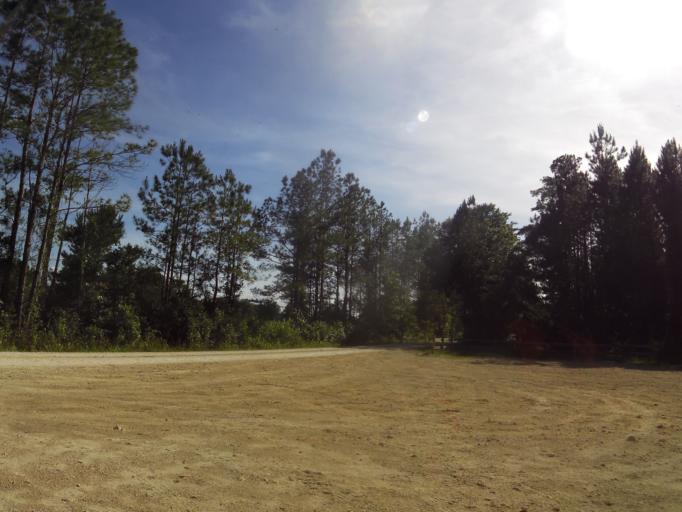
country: US
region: Florida
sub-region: Nassau County
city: Callahan
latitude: 30.5780
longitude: -81.7669
